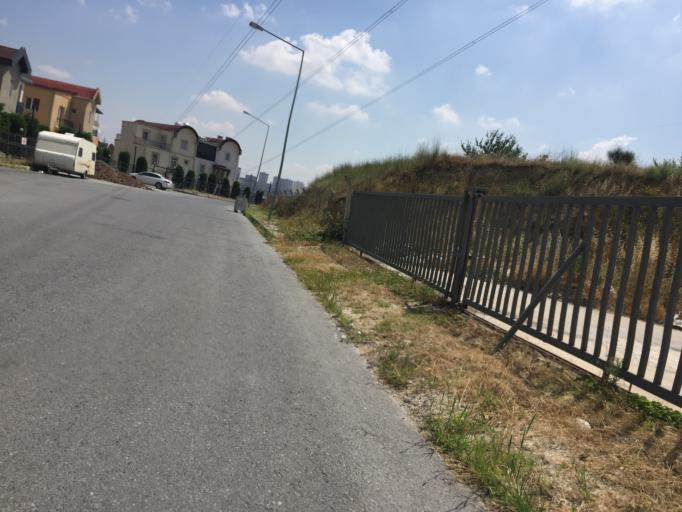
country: TR
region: Istanbul
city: Esenyurt
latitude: 41.0785
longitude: 28.6697
